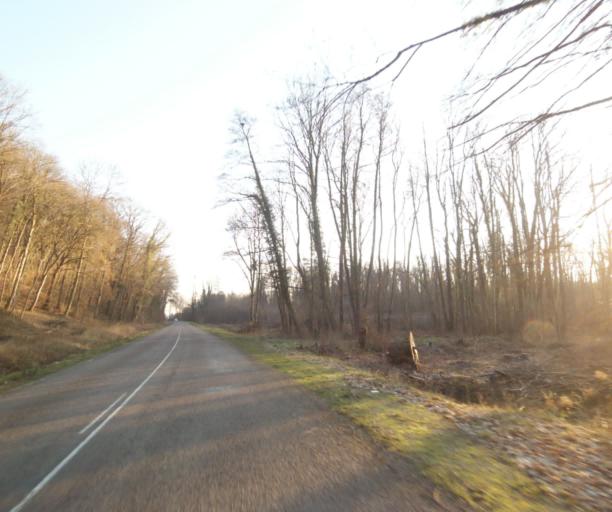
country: FR
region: Champagne-Ardenne
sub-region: Departement de la Haute-Marne
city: Chevillon
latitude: 48.5318
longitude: 5.1067
